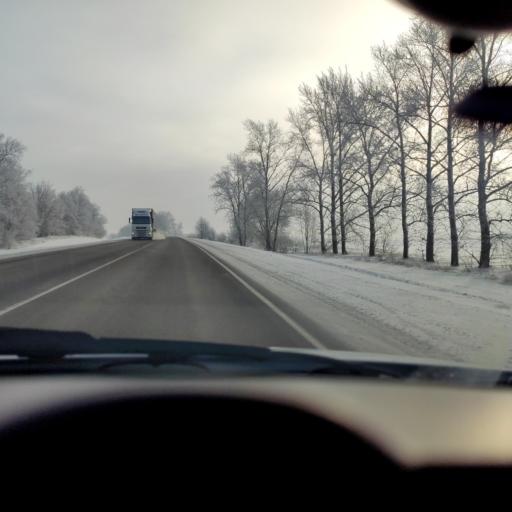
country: RU
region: Kursk
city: Kirovskiy
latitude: 51.6950
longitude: 36.5301
